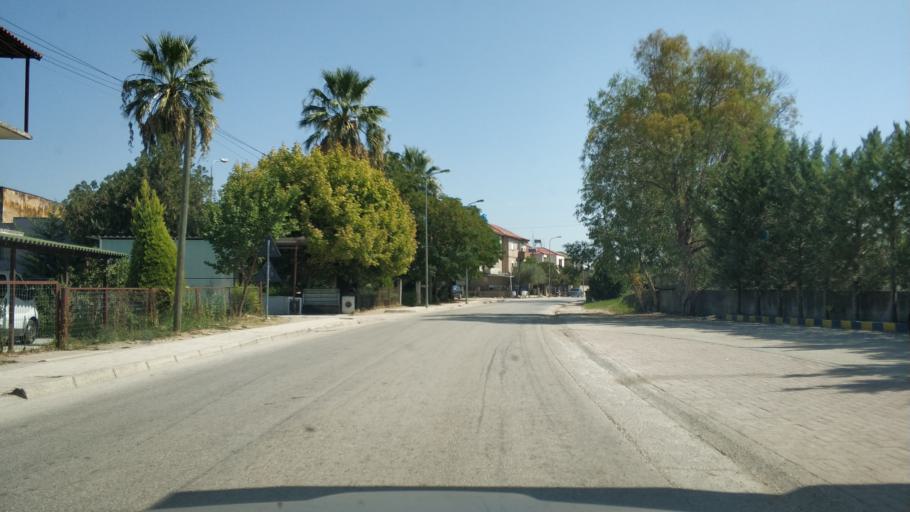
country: AL
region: Fier
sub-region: Rrethi i Lushnjes
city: Gradishte
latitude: 40.8939
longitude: 19.6319
